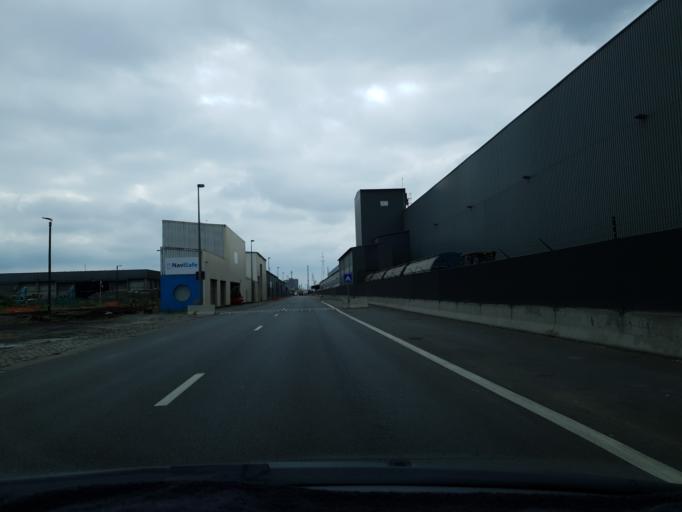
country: BE
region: Flanders
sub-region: Provincie Antwerpen
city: Antwerpen
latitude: 51.2579
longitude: 4.3801
